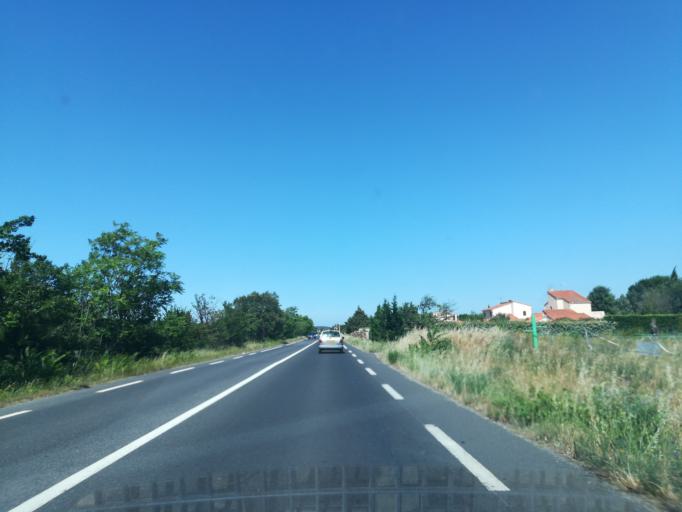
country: FR
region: Languedoc-Roussillon
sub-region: Departement des Pyrenees-Orientales
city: Sant Joan de Pladecorts
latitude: 42.5079
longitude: 2.7714
